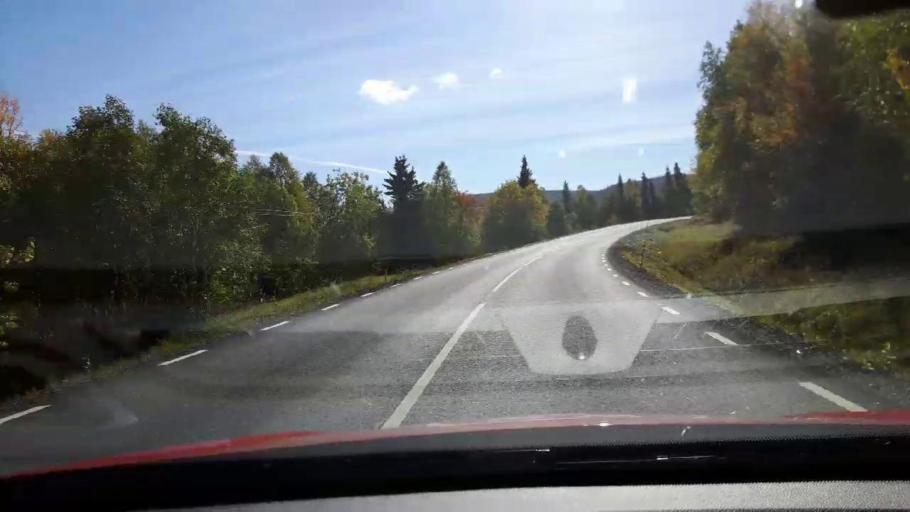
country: NO
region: Nord-Trondelag
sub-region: Royrvik
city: Royrvik
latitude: 64.8751
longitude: 14.2113
